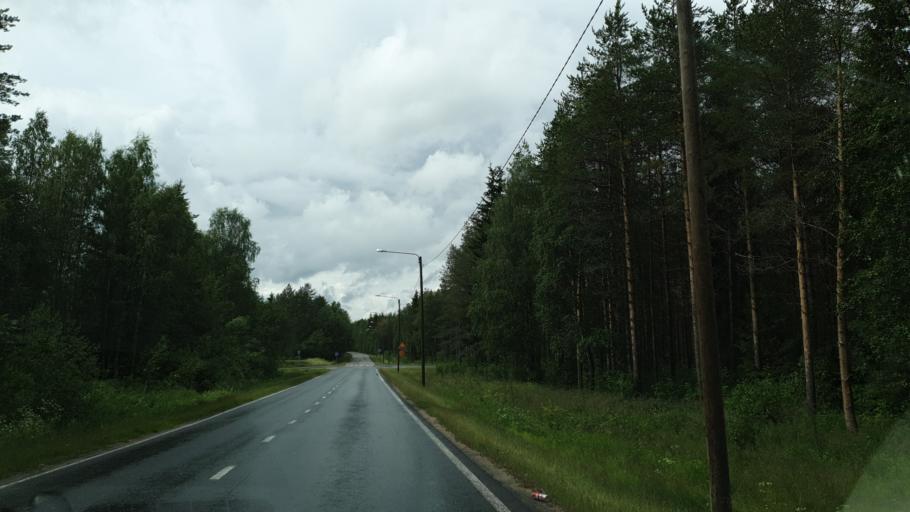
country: FI
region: Kainuu
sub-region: Kehys-Kainuu
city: Kuhmo
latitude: 64.1174
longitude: 29.4882
